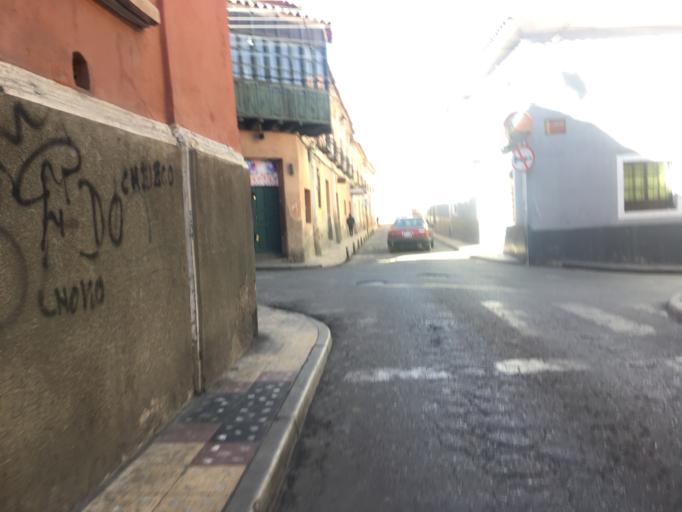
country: BO
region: Potosi
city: Potosi
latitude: -19.5889
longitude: -65.7554
